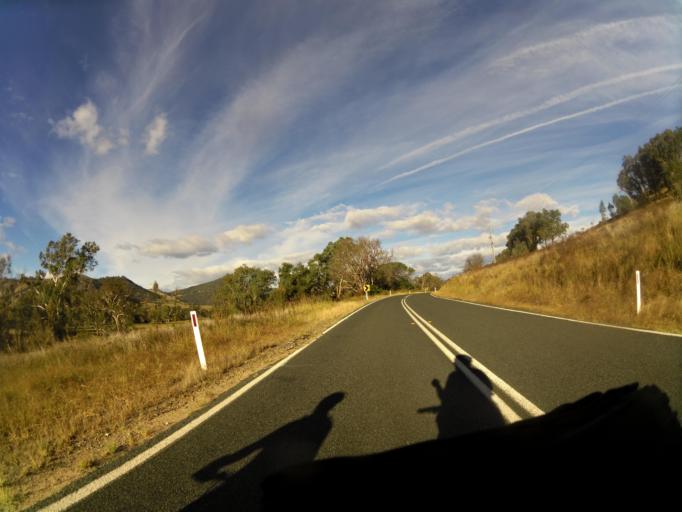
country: AU
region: New South Wales
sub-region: Greater Hume Shire
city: Holbrook
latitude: -35.9935
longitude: 147.8624
